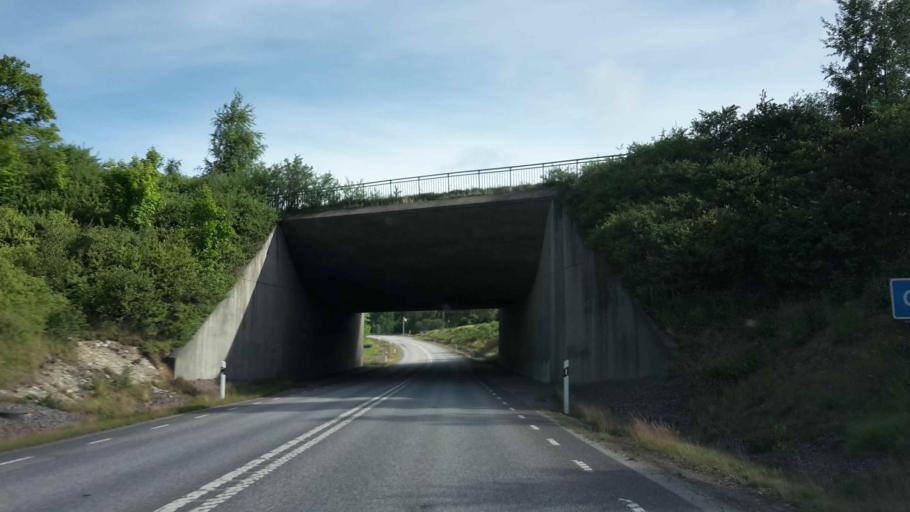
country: SE
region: OEstergoetland
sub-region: Motala Kommun
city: Borensberg
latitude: 58.5500
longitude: 15.3213
